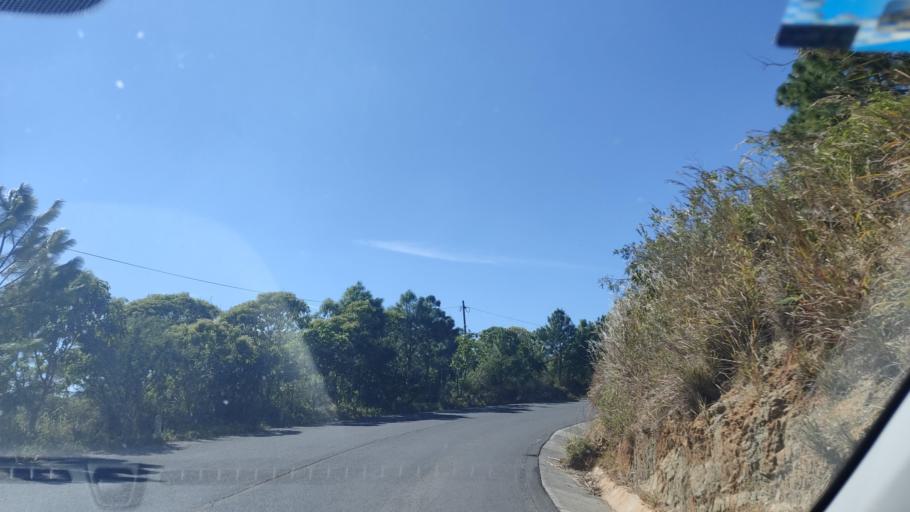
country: MX
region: Nayarit
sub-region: Jala
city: Rosa Blanca
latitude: 21.0968
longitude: -104.3806
